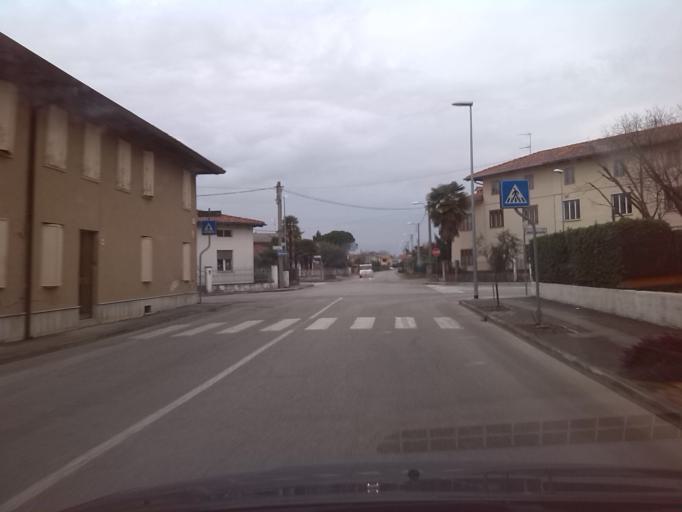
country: IT
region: Friuli Venezia Giulia
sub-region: Provincia di Gorizia
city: Romans d'Isonzo
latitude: 45.8939
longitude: 13.4376
